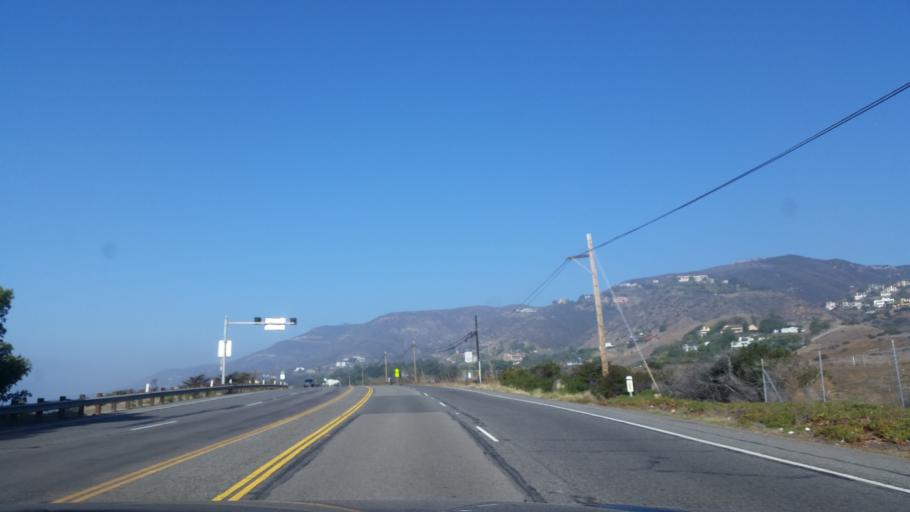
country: US
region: California
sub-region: Los Angeles County
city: Malibu
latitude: 34.0326
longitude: -118.8456
